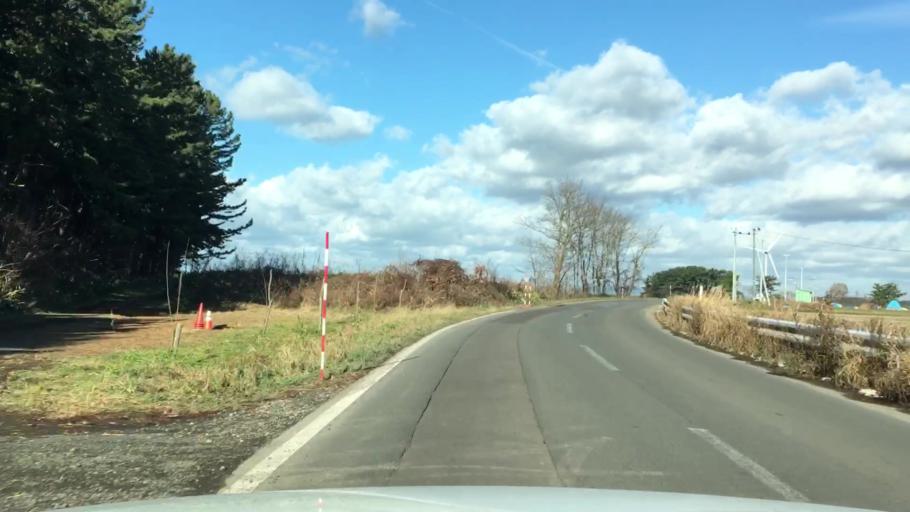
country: JP
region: Aomori
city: Shimokizukuri
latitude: 40.8523
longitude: 140.3002
